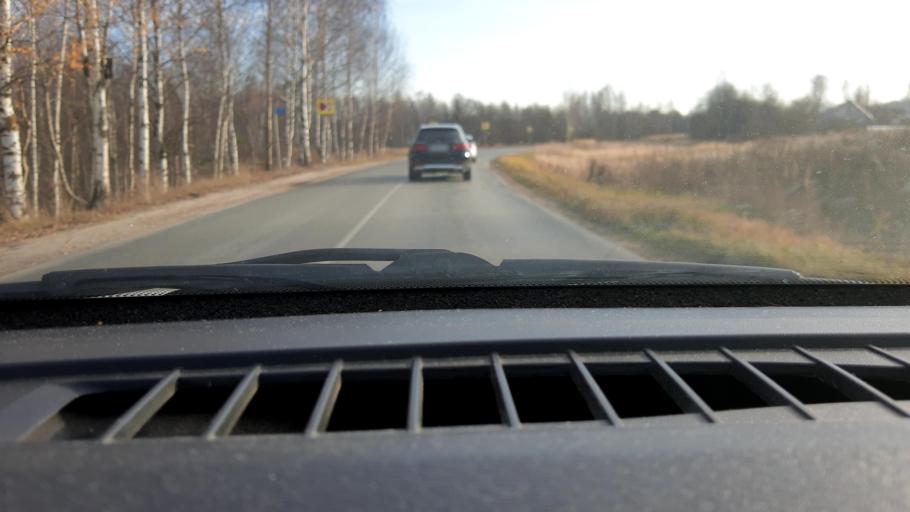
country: RU
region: Nizjnij Novgorod
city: Neklyudovo
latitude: 56.4372
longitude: 43.9198
